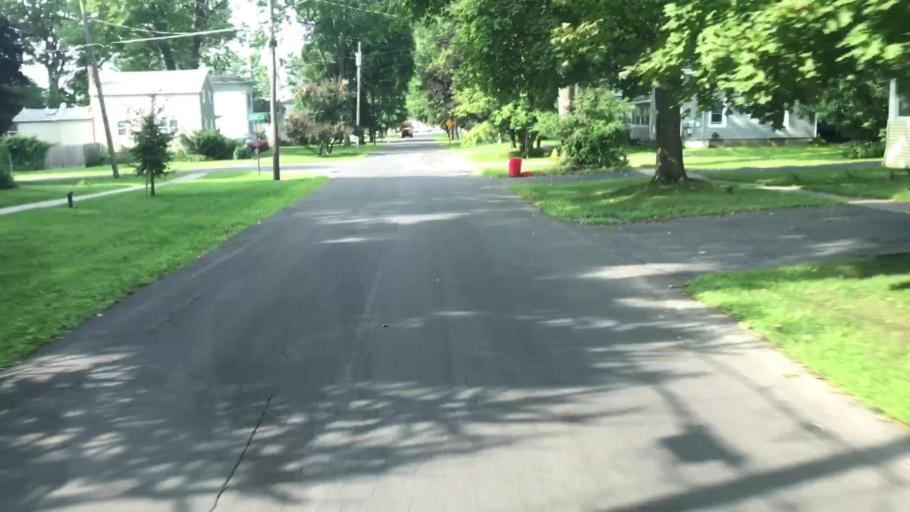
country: US
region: New York
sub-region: Onondaga County
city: Liverpool
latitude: 43.1065
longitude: -76.2052
